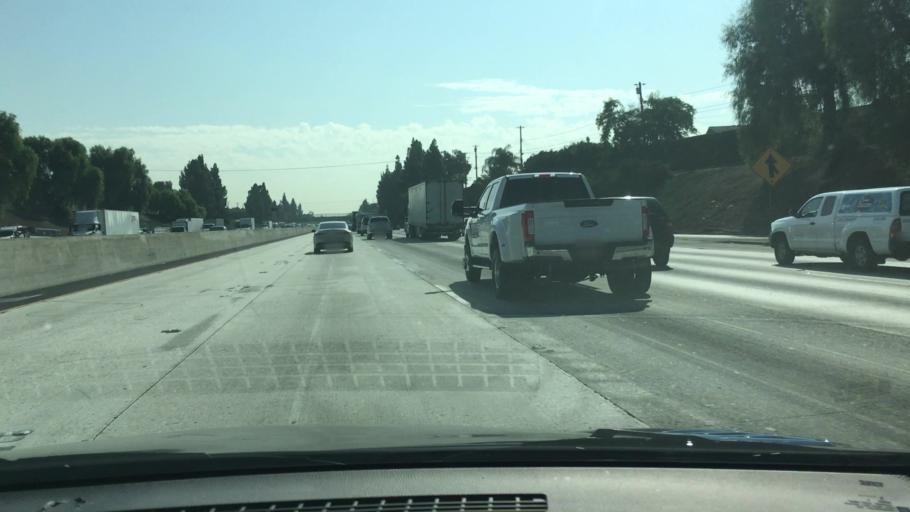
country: US
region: California
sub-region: San Bernardino County
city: Chino
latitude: 34.0301
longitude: -117.7050
